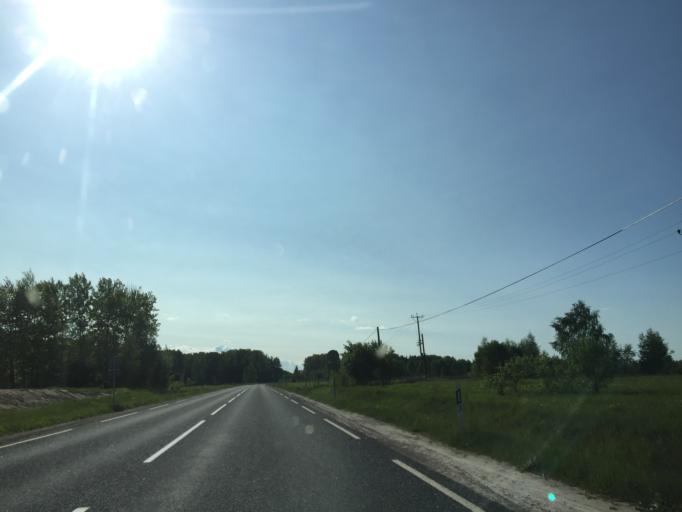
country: LV
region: Salaspils
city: Salaspils
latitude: 56.8219
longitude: 24.4037
